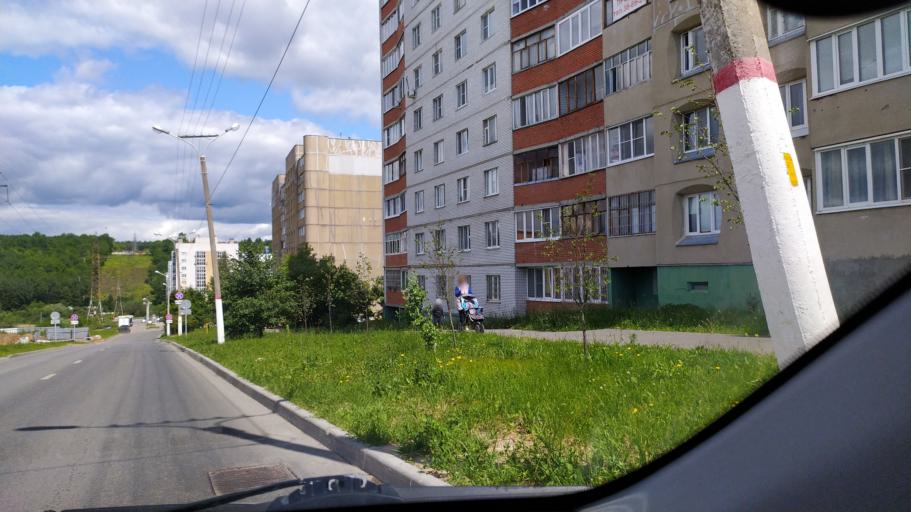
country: RU
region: Chuvashia
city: Novyye Lapsary
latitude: 56.1197
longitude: 47.1749
